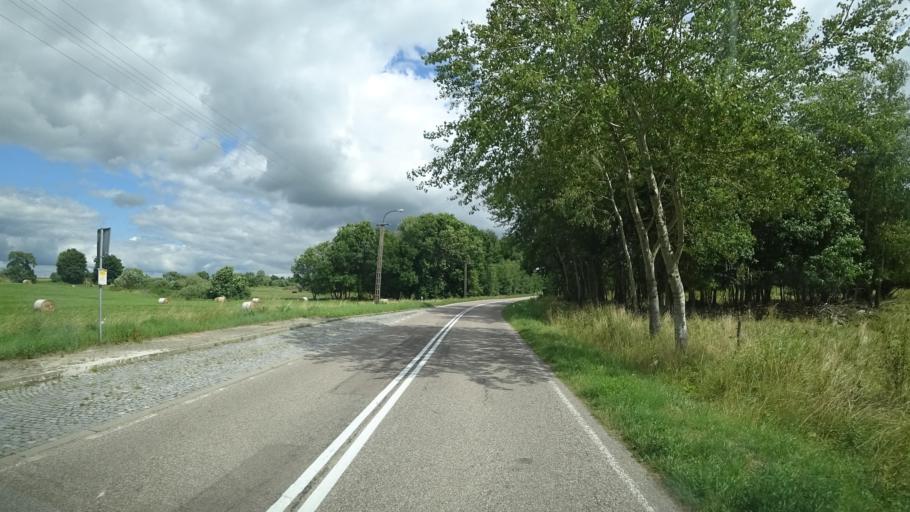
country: PL
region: Warmian-Masurian Voivodeship
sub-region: Powiat goldapski
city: Goldap
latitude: 54.2084
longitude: 22.1917
